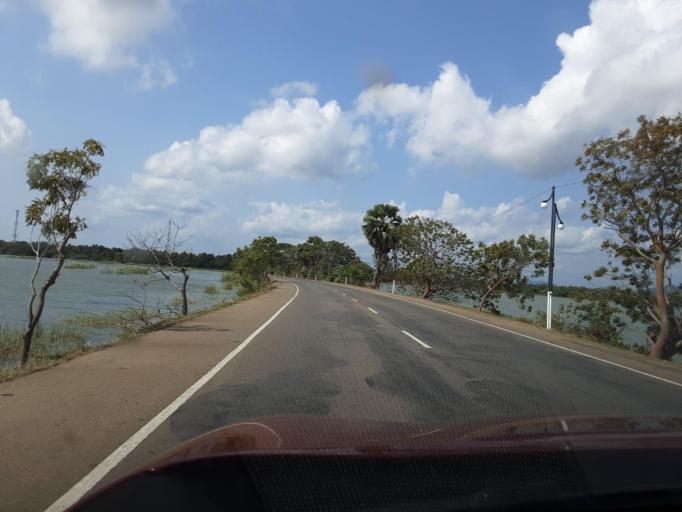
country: LK
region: Southern
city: Tangalla
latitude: 6.2892
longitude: 81.2342
